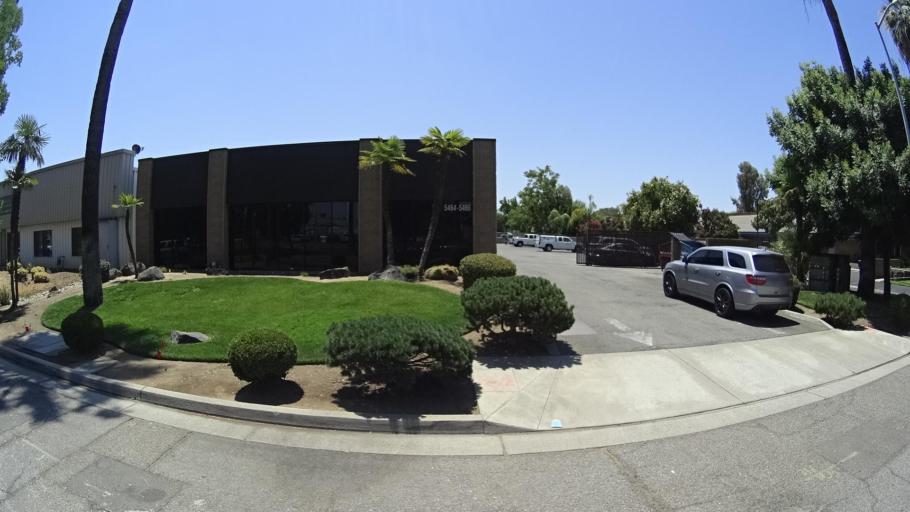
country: US
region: California
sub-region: Fresno County
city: Sunnyside
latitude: 36.7607
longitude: -119.7063
